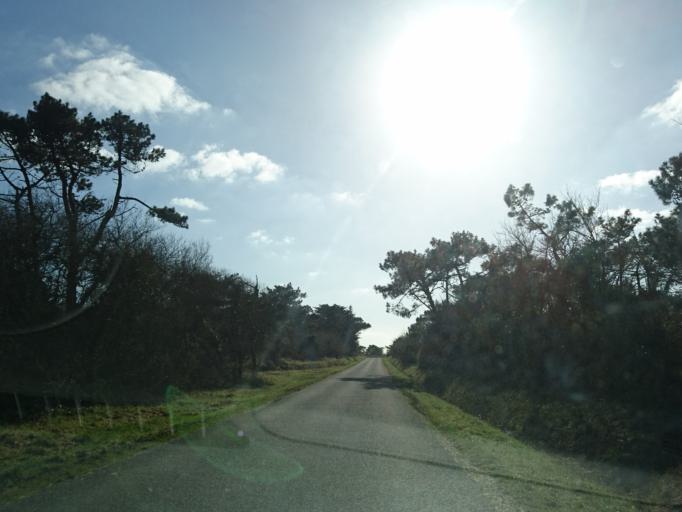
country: FR
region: Brittany
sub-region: Departement du Finistere
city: Roscanvel
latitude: 48.3244
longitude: -4.5741
